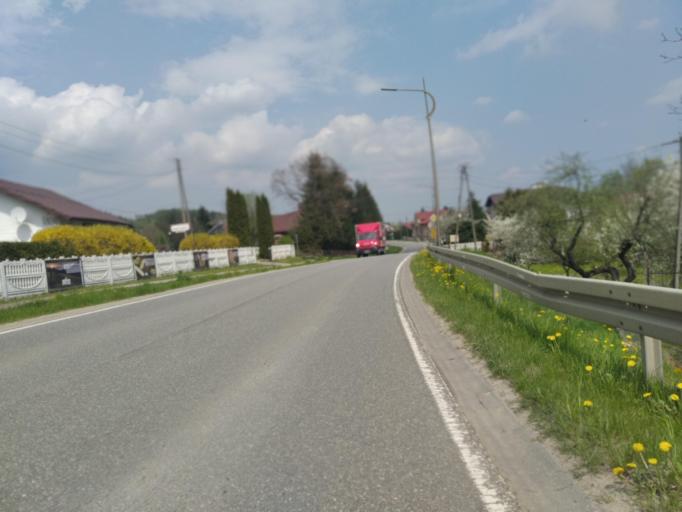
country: PL
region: Subcarpathian Voivodeship
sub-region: Powiat krosnienski
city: Rymanow
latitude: 49.5569
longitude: 21.8549
